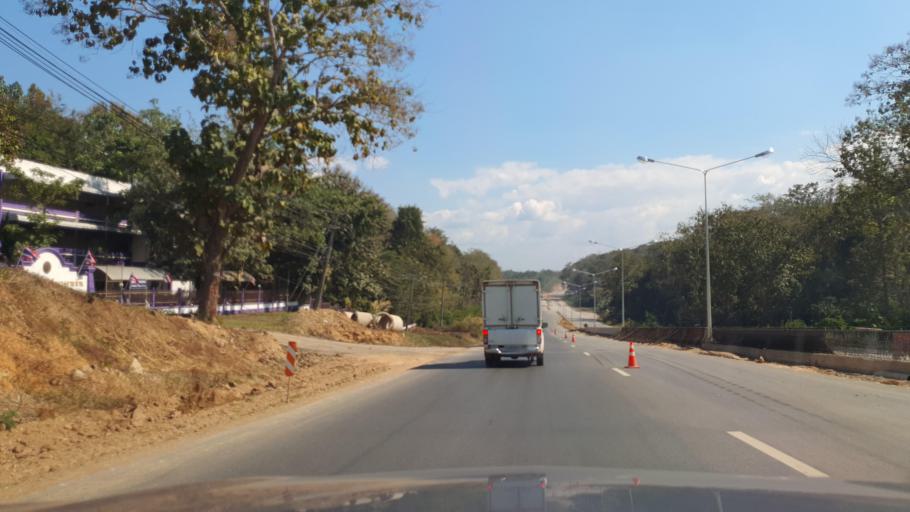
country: TH
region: Nan
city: Nan
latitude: 18.8302
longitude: 100.7534
